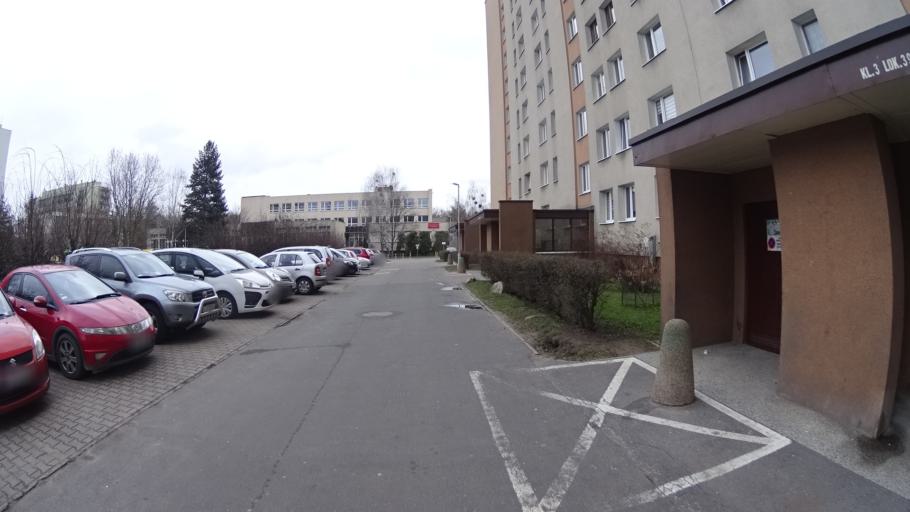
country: PL
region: Masovian Voivodeship
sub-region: Warszawa
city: Bemowo
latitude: 52.2514
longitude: 20.9265
